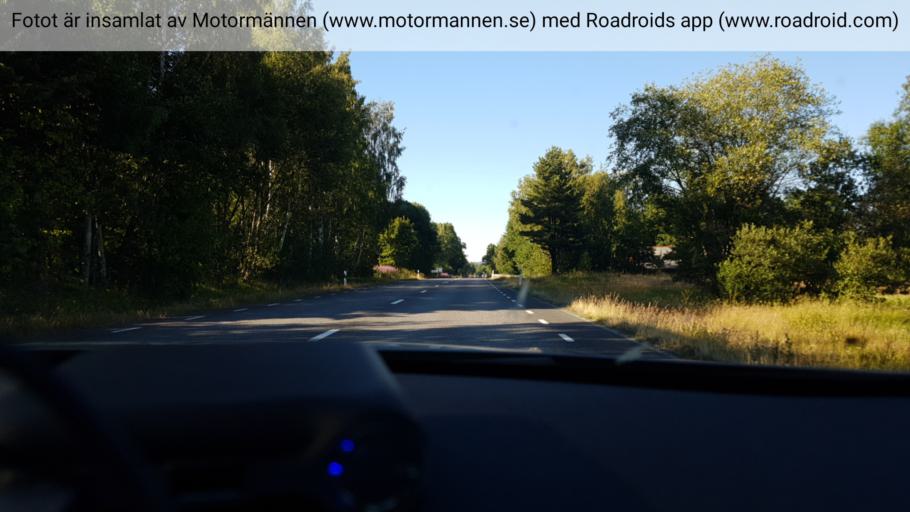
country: SE
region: Joenkoeping
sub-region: Habo Kommun
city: Habo
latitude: 57.9436
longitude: 14.1001
